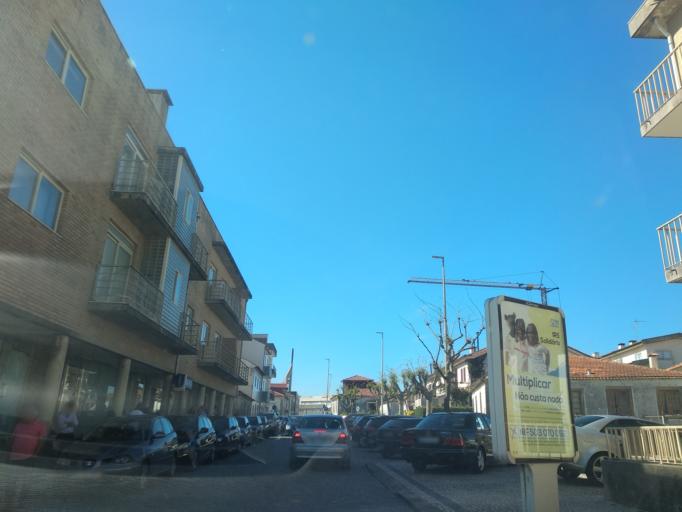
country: PT
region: Braga
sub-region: Esposende
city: Apulia
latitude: 41.4837
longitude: -8.7770
